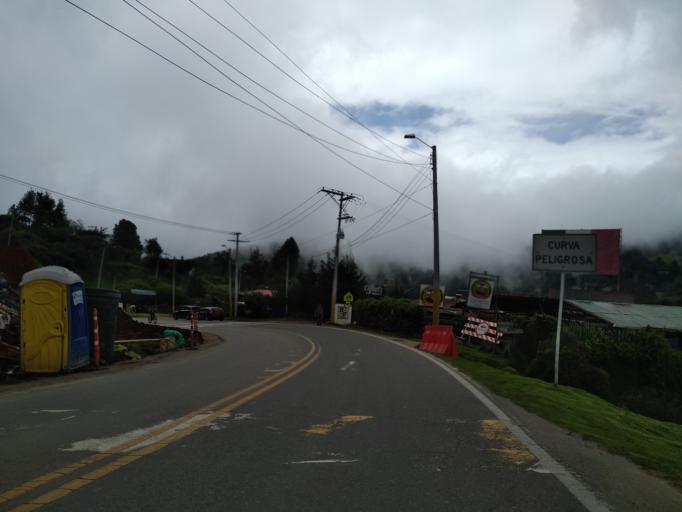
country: CO
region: Bogota D.C.
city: Barrio San Luis
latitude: 4.6615
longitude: -74.0084
